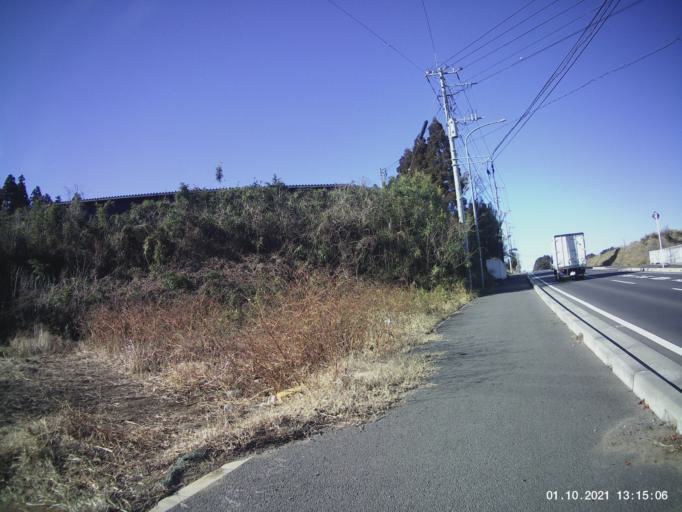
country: JP
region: Chiba
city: Yotsukaido
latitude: 35.6150
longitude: 140.1986
